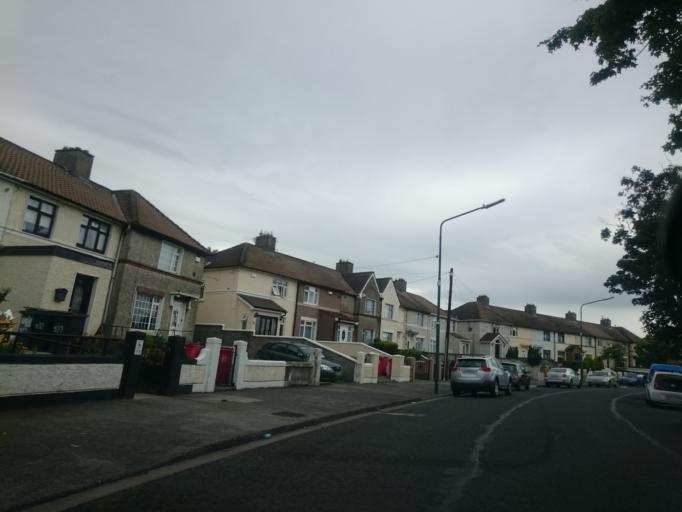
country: IE
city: Greenhills
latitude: 53.3217
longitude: -6.2999
